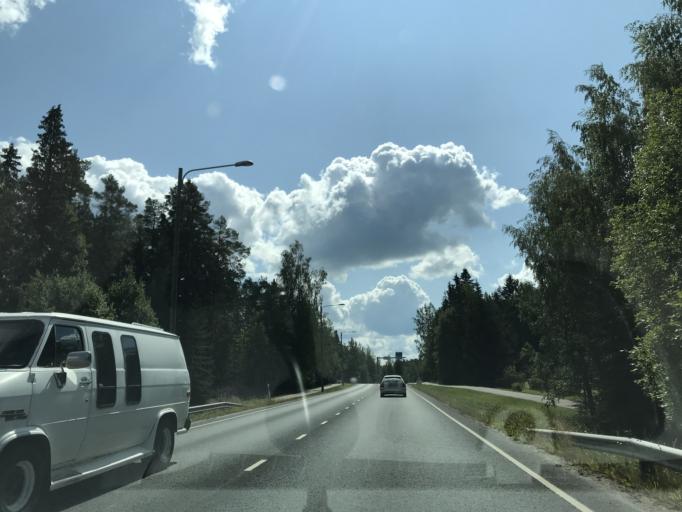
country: FI
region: Paijanne Tavastia
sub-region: Lahti
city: Orimattila
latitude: 60.8211
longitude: 25.7296
